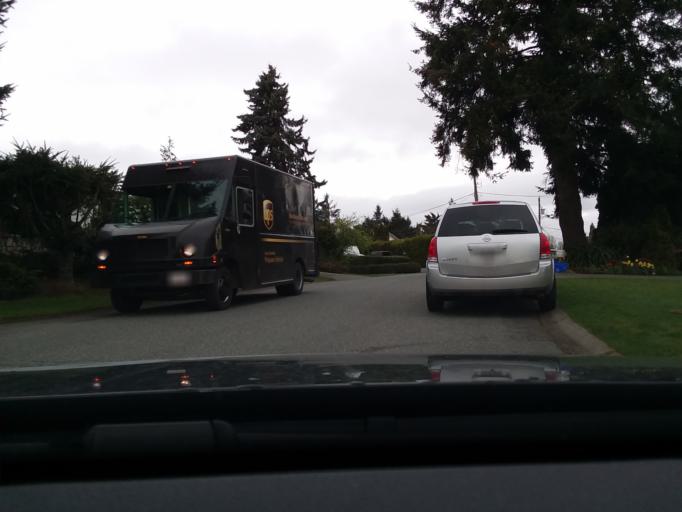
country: CA
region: British Columbia
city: North Saanich
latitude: 48.5629
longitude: -123.3990
